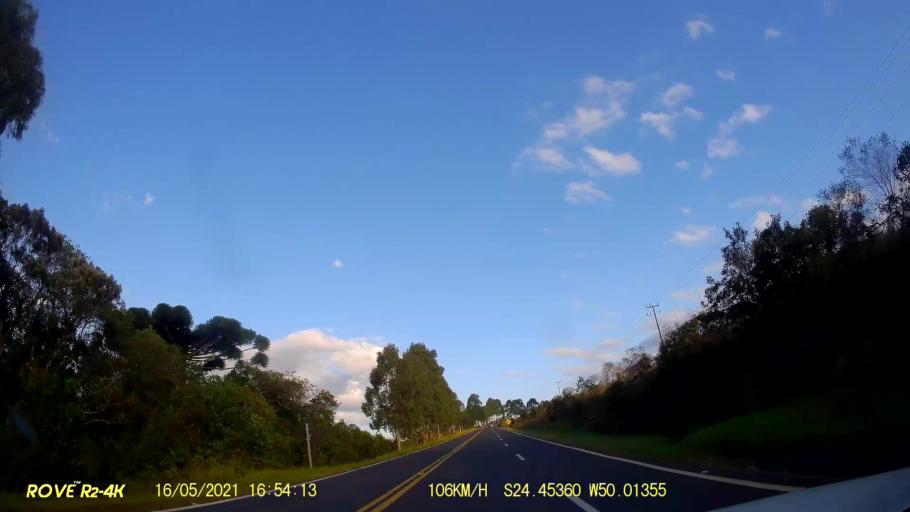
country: BR
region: Parana
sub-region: Pirai Do Sul
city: Pirai do Sul
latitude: -24.4538
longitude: -50.0136
